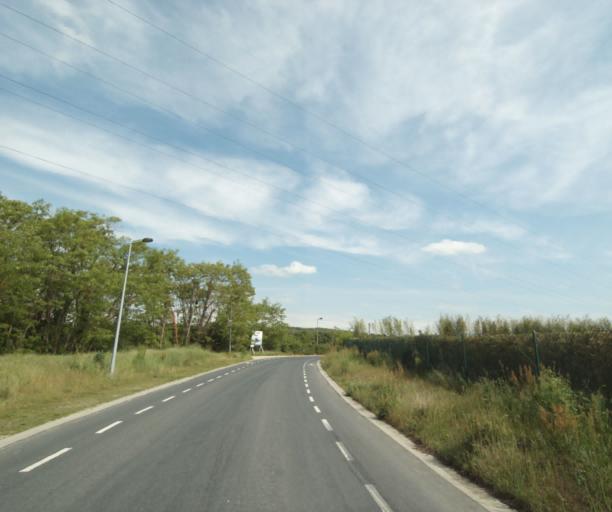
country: FR
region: Ile-de-France
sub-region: Departement des Yvelines
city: Mezy-sur-Seine
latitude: 48.9913
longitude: 1.8917
